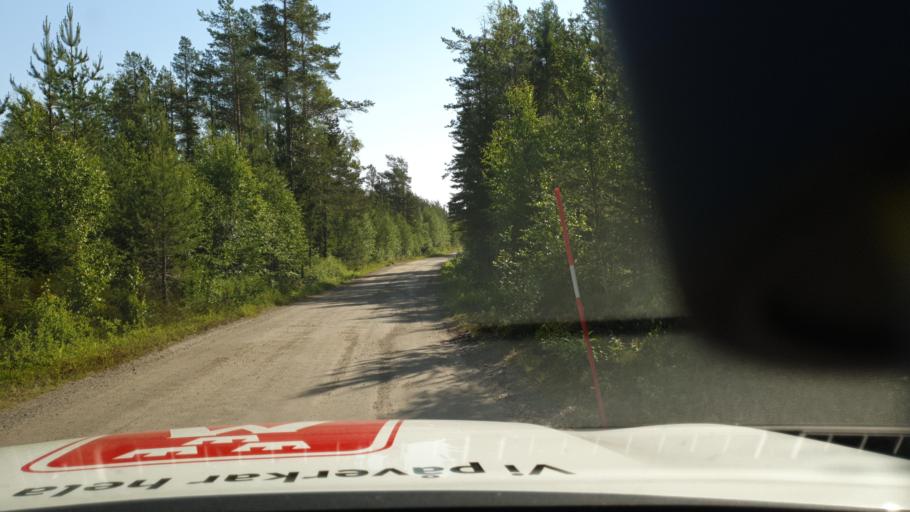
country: SE
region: Vaesterbotten
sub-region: Robertsfors Kommun
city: Robertsfors
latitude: 64.2280
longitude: 21.0477
